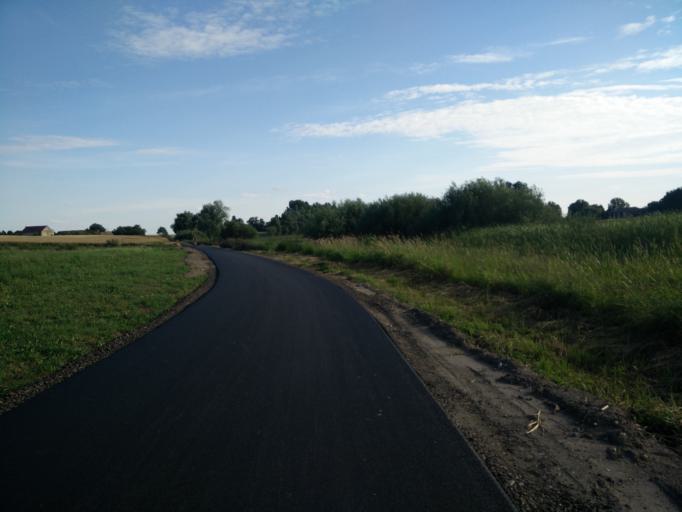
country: PL
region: Greater Poland Voivodeship
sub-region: Powiat sredzki
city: Sroda Wielkopolska
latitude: 52.2477
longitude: 17.2982
